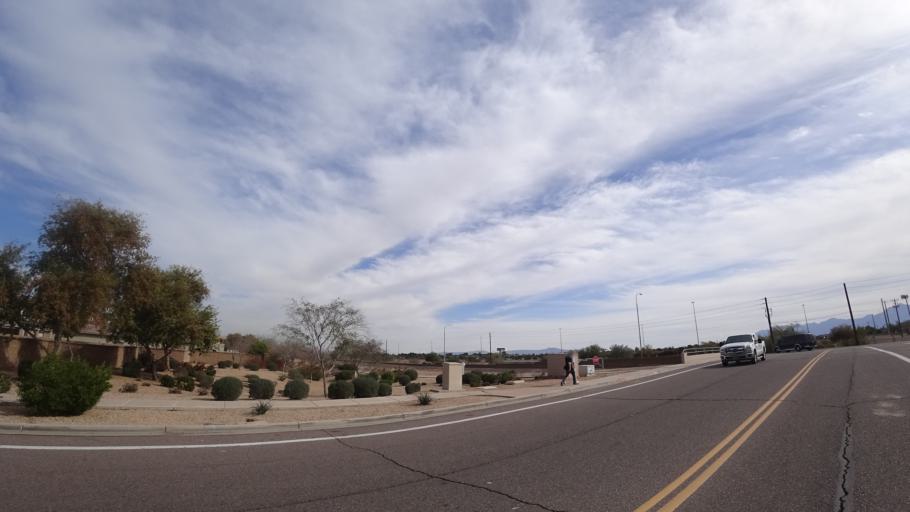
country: US
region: Arizona
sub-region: Maricopa County
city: Tolleson
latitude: 33.4655
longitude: -112.2639
